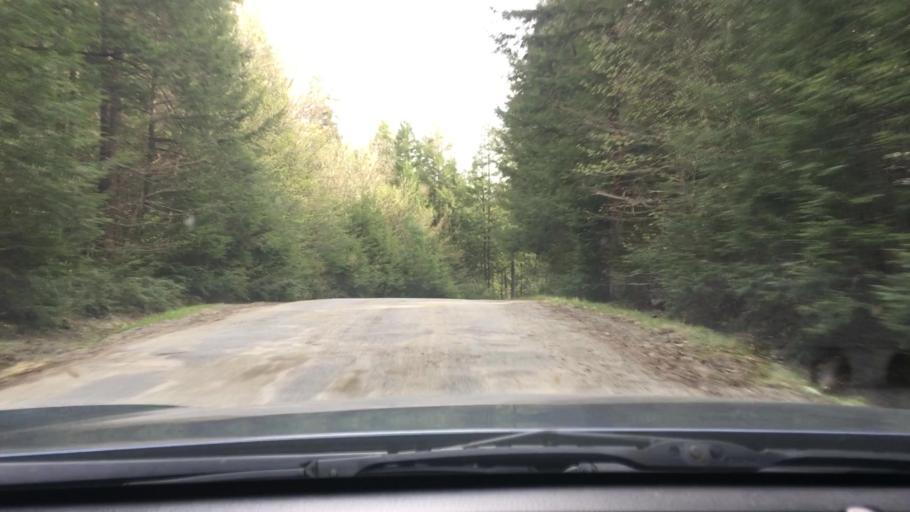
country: US
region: New York
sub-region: Warren County
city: Warrensburg
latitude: 43.8151
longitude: -73.7455
